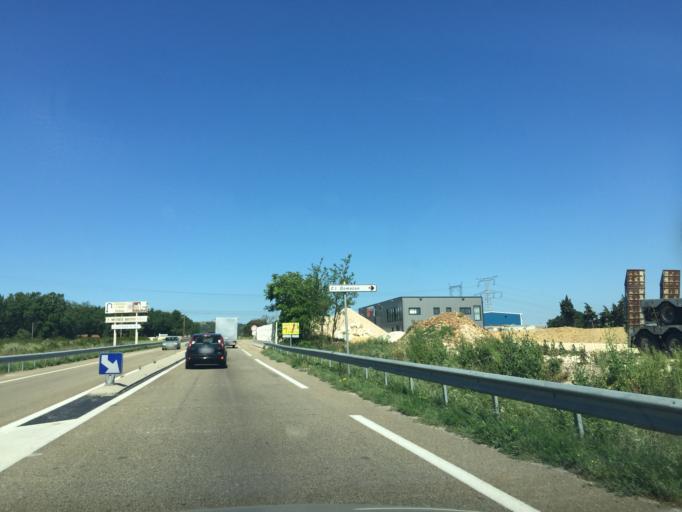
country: FR
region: Languedoc-Roussillon
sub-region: Departement du Gard
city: Saze
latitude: 43.9513
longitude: 4.6684
